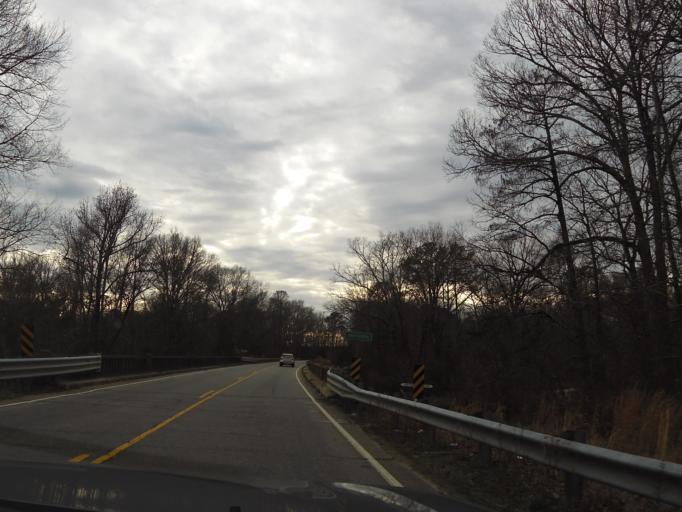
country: US
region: North Carolina
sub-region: Edgecombe County
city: Tarboro
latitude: 35.9808
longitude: -77.5936
